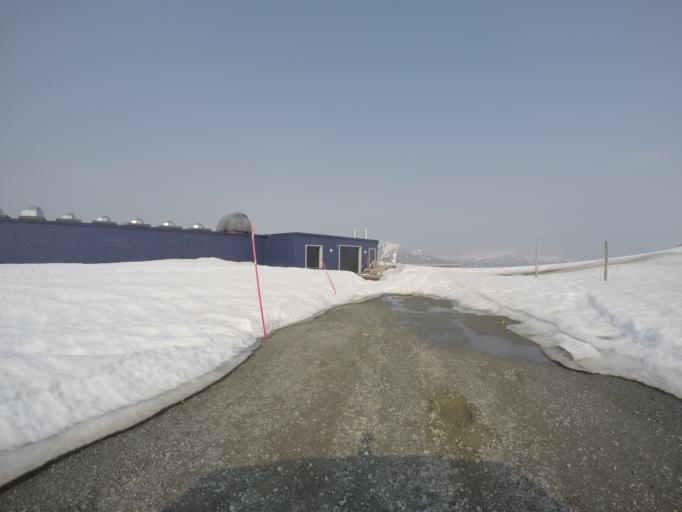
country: SJ
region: Svalbard
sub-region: Spitsbergen
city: Longyearbyen
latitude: 78.1498
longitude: 16.0333
